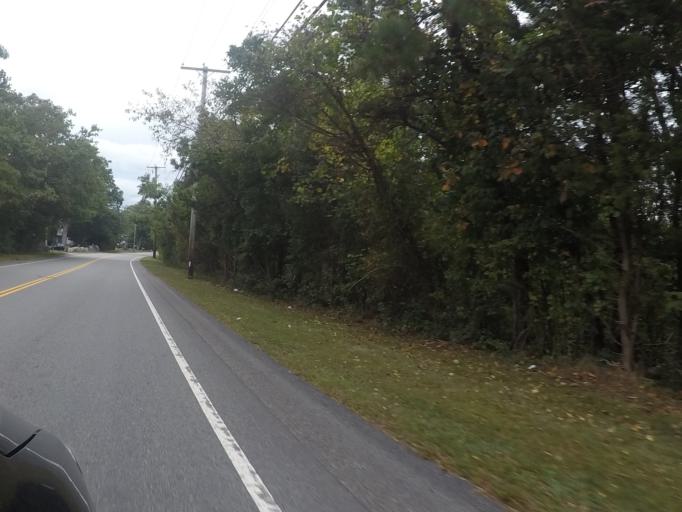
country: US
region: Massachusetts
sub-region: Bristol County
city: Smith Mills
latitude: 41.5898
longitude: -71.0012
